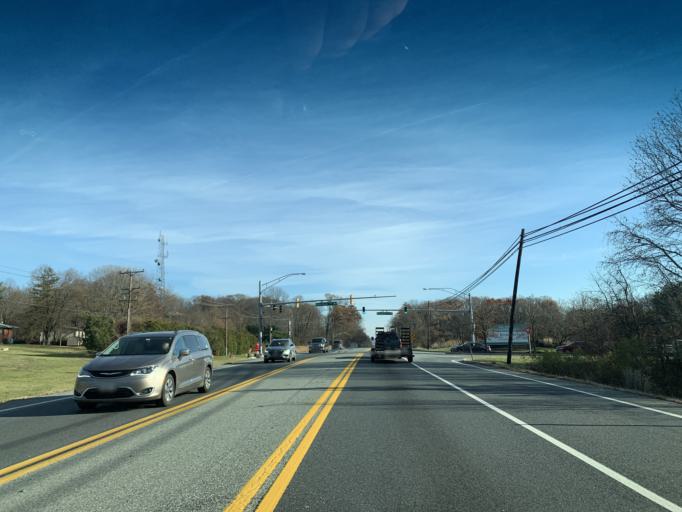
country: US
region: Maryland
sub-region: Harford County
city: Havre de Grace
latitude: 39.5685
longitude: -76.1317
